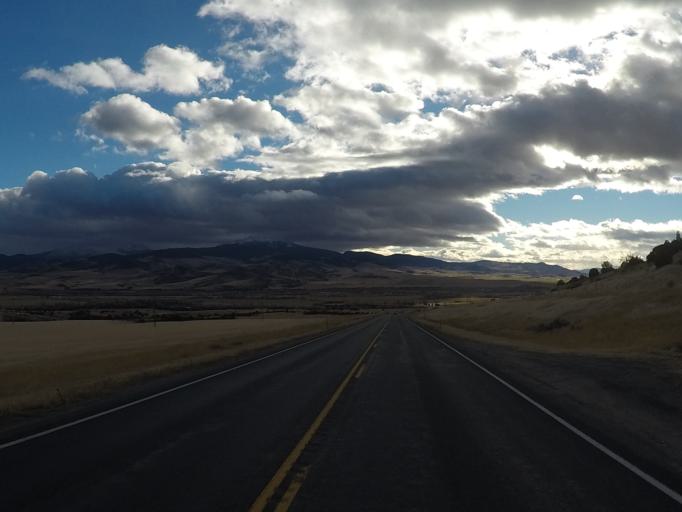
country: US
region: Montana
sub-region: Jefferson County
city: Whitehall
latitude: 45.8870
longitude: -111.9685
